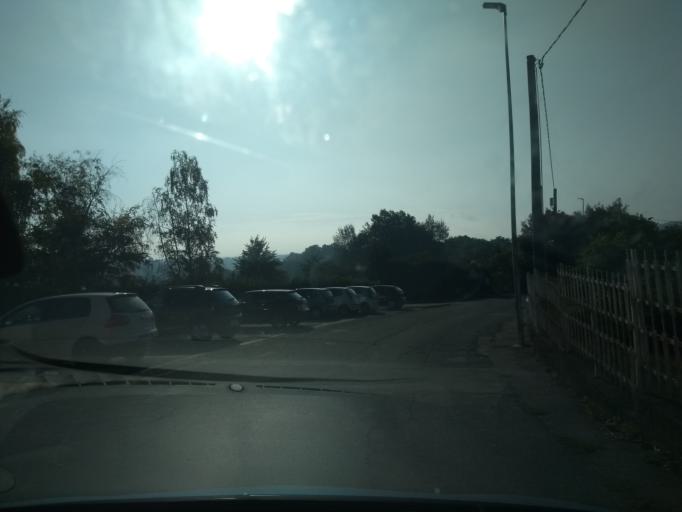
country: IT
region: Piedmont
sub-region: Provincia di Torino
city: Vallo Torinese
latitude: 45.2233
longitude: 7.4991
